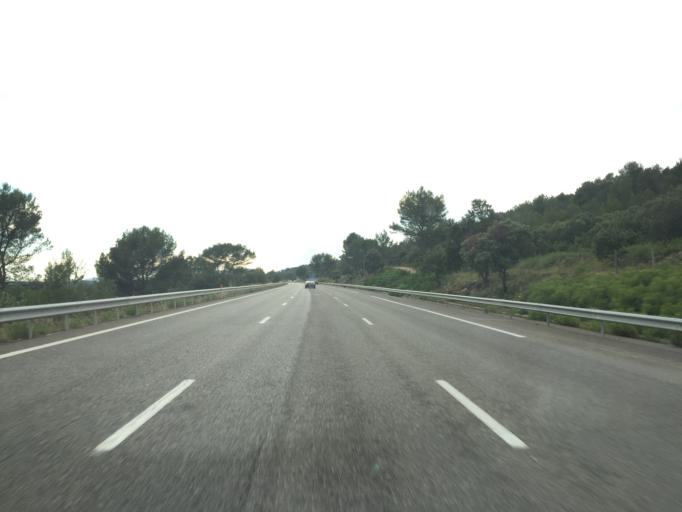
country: FR
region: Provence-Alpes-Cote d'Azur
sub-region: Departement du Var
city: La Celle
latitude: 43.4209
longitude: 6.0136
